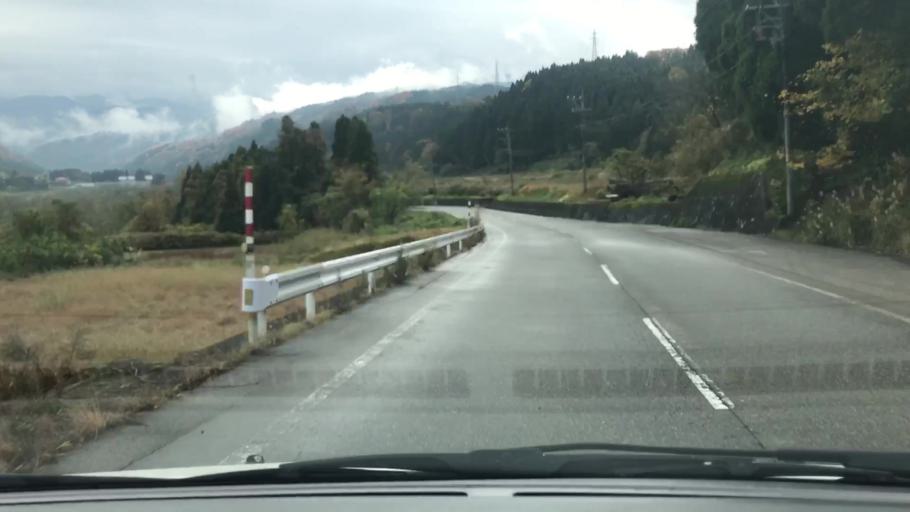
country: JP
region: Toyama
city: Kamiichi
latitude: 36.5903
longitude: 137.3182
